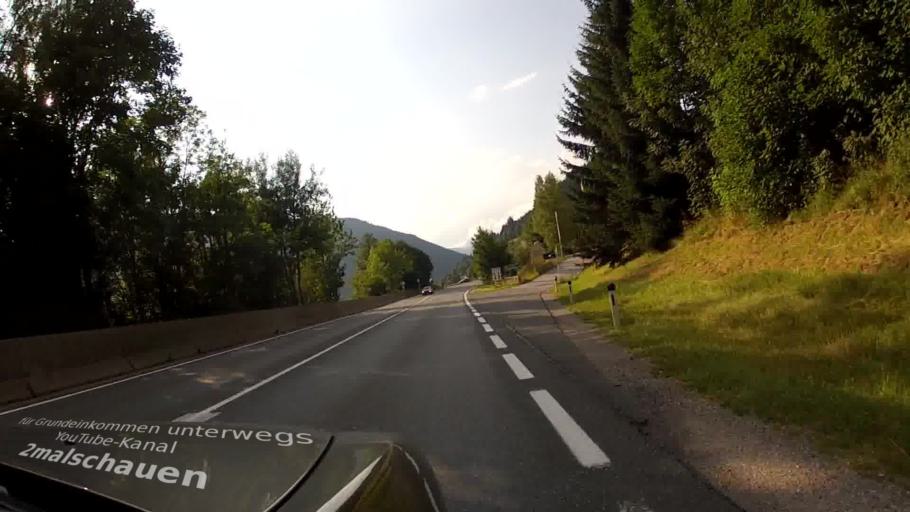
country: AT
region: Salzburg
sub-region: Politischer Bezirk Sankt Johann im Pongau
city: Altenmarkt im Pongau
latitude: 47.3877
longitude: 13.4135
